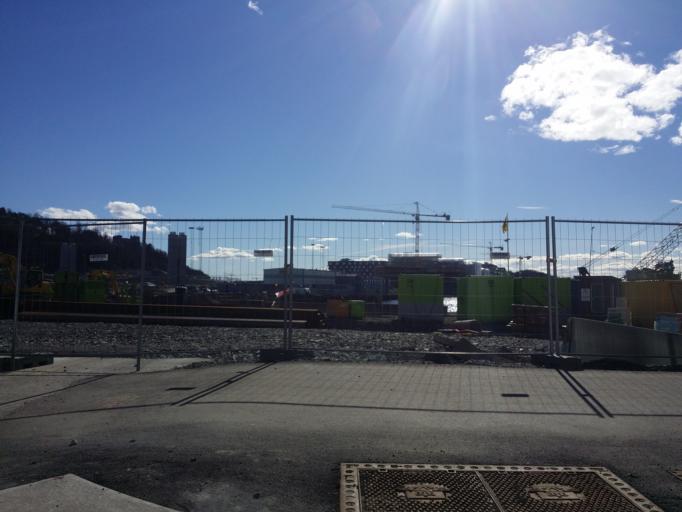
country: NO
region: Oslo
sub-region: Oslo
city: Oslo
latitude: 59.9070
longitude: 10.7604
